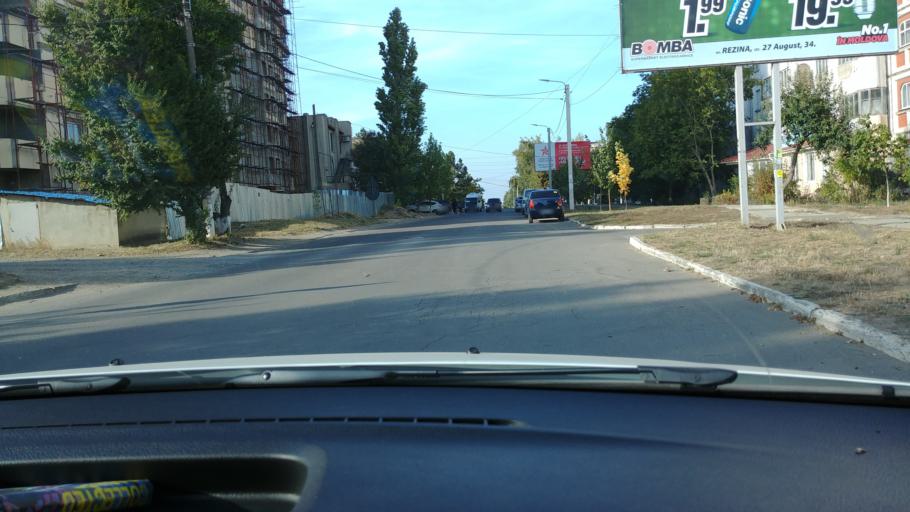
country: MD
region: Rezina
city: Rezina
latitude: 47.7477
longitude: 28.9562
